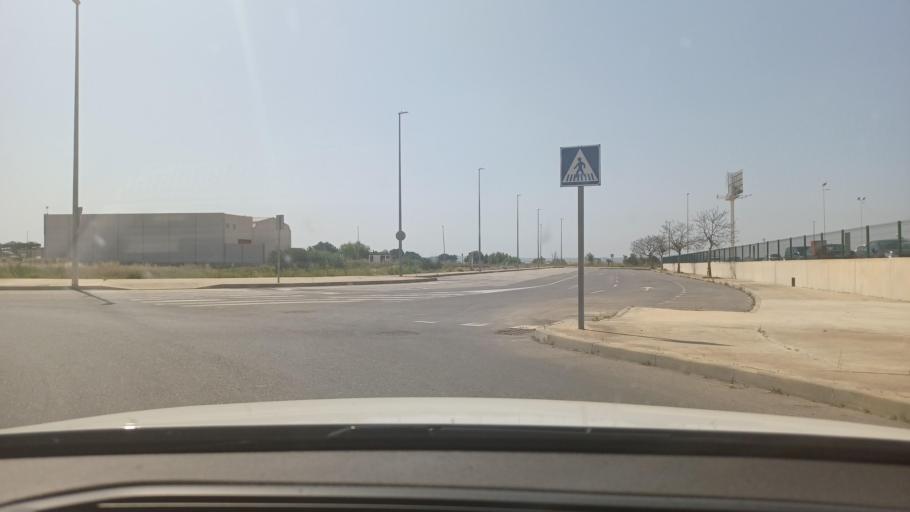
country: ES
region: Valencia
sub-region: Provincia de Alicante
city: Dolores
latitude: 38.1429
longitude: -0.7458
